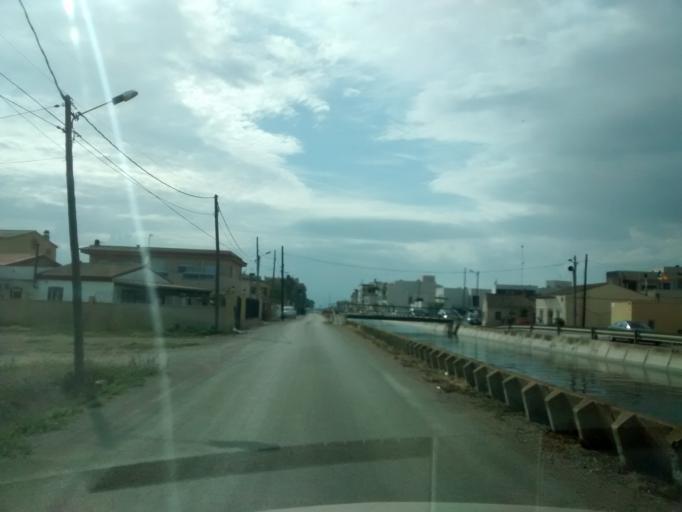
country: ES
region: Catalonia
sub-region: Provincia de Tarragona
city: Deltebre
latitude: 40.7032
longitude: 0.7212
